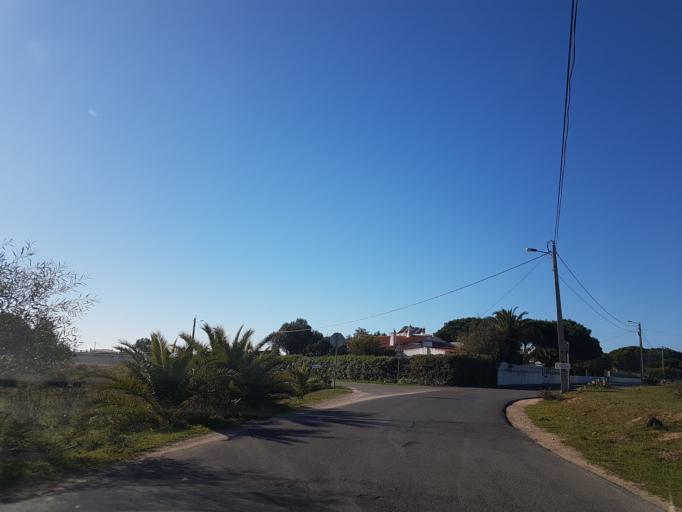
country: PT
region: Faro
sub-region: Silves
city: Armacao de Pera
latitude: 37.1164
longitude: -8.4034
